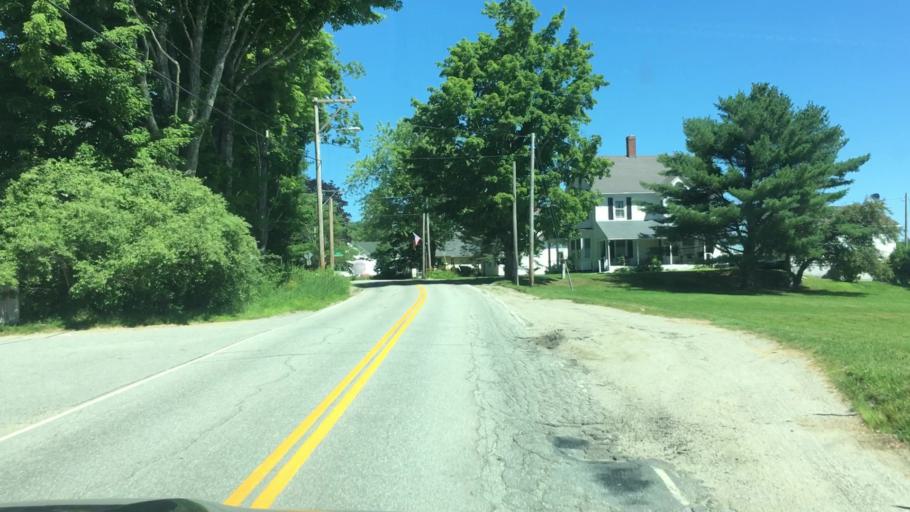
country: US
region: Maine
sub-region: Hancock County
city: Penobscot
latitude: 44.4544
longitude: -68.7025
